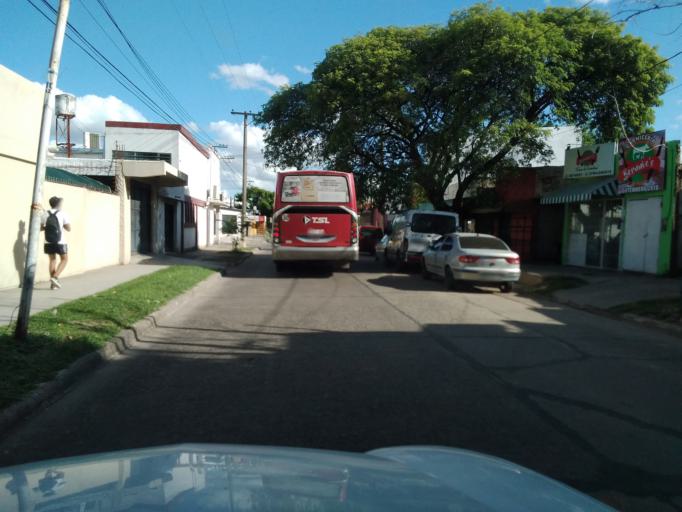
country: AR
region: Corrientes
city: Corrientes
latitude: -27.4906
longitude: -58.8330
